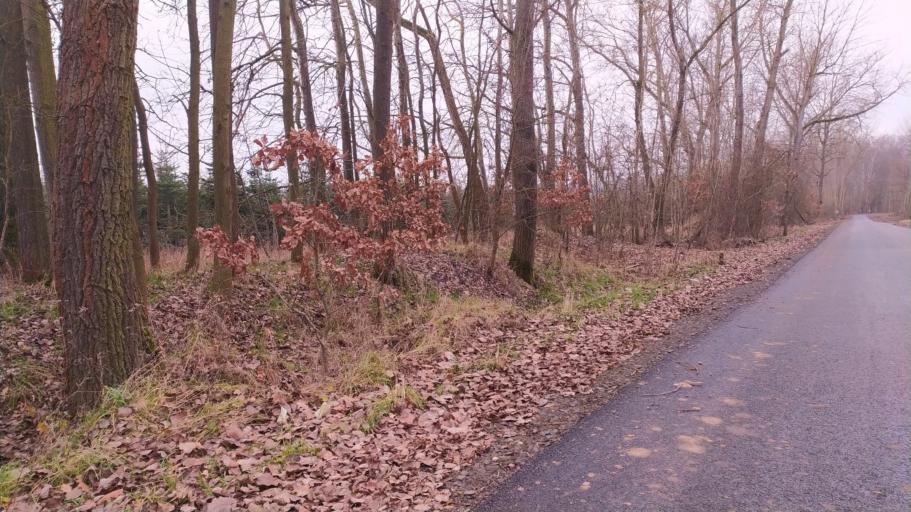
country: DE
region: Bavaria
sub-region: Upper Franconia
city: Schirnding
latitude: 50.1013
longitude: 12.2700
